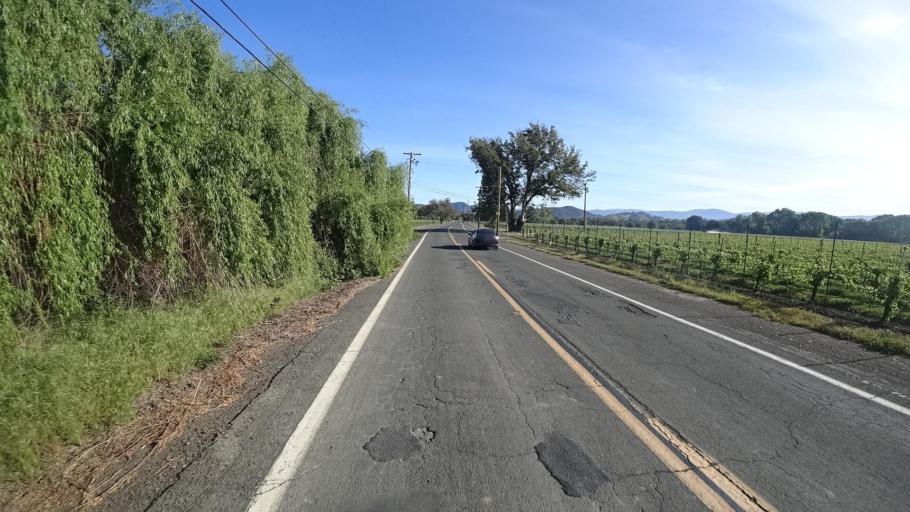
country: US
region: California
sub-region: Lake County
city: Lakeport
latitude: 39.0654
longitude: -122.9497
